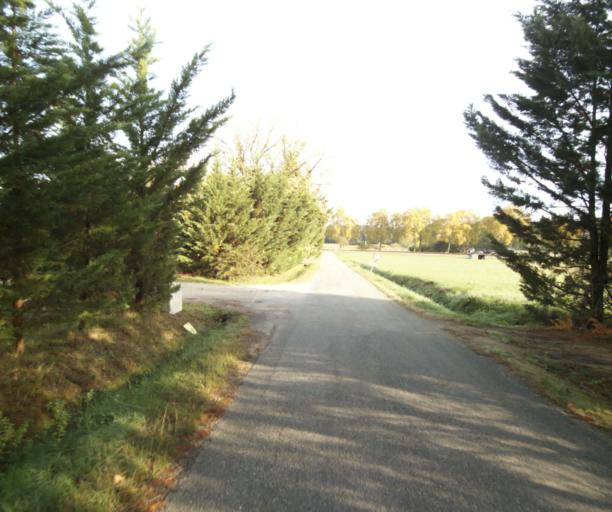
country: FR
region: Midi-Pyrenees
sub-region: Departement de la Haute-Garonne
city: Villemur-sur-Tarn
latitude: 43.9266
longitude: 1.5046
